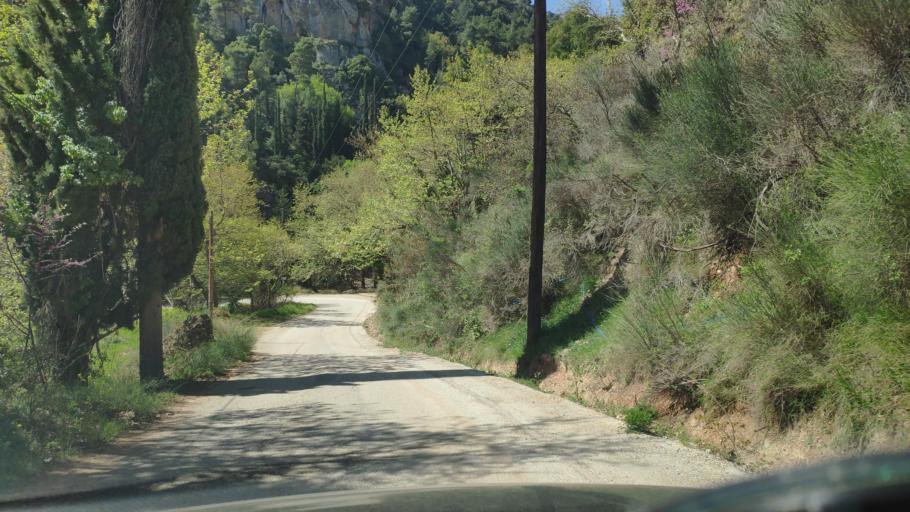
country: GR
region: West Greece
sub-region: Nomos Achaias
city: Akrata
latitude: 38.0959
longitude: 22.3175
